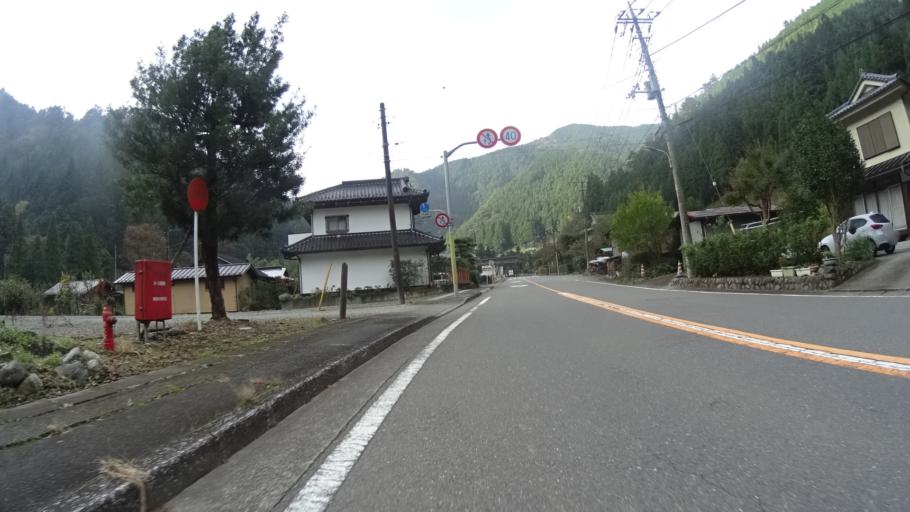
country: JP
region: Tokyo
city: Itsukaichi
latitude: 35.7158
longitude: 139.1516
